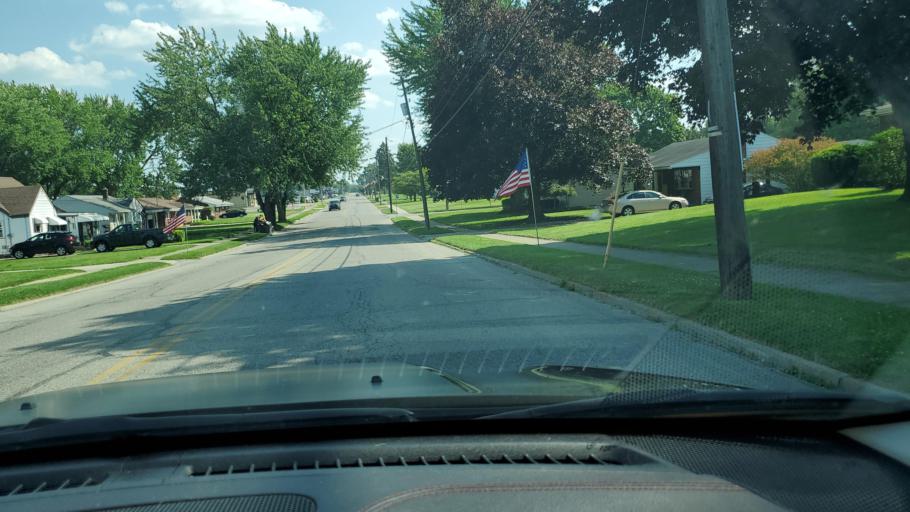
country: US
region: Ohio
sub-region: Mahoning County
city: Struthers
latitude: 41.0472
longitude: -80.6035
